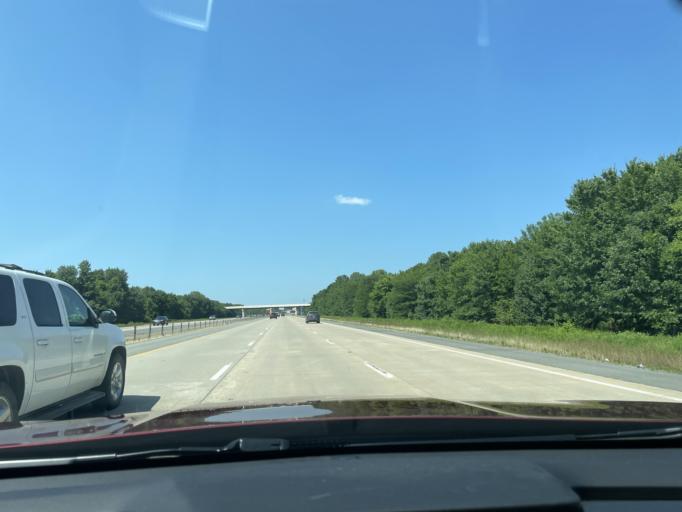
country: US
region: Arkansas
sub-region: Pulaski County
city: Gravel Ridge
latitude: 34.8439
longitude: -92.1539
